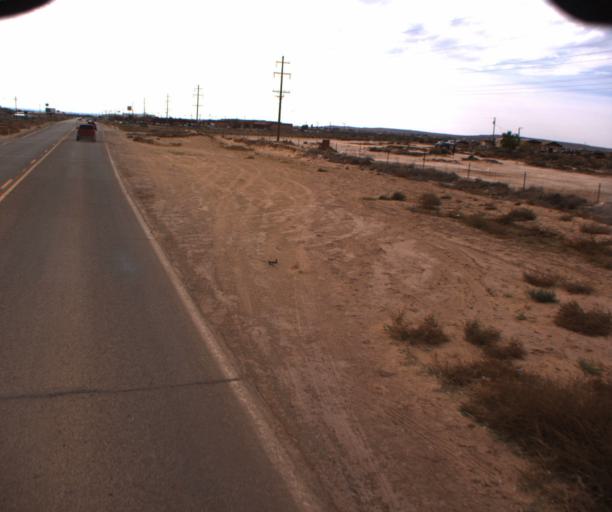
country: US
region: Arizona
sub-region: Apache County
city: Chinle
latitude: 36.1684
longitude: -109.5861
